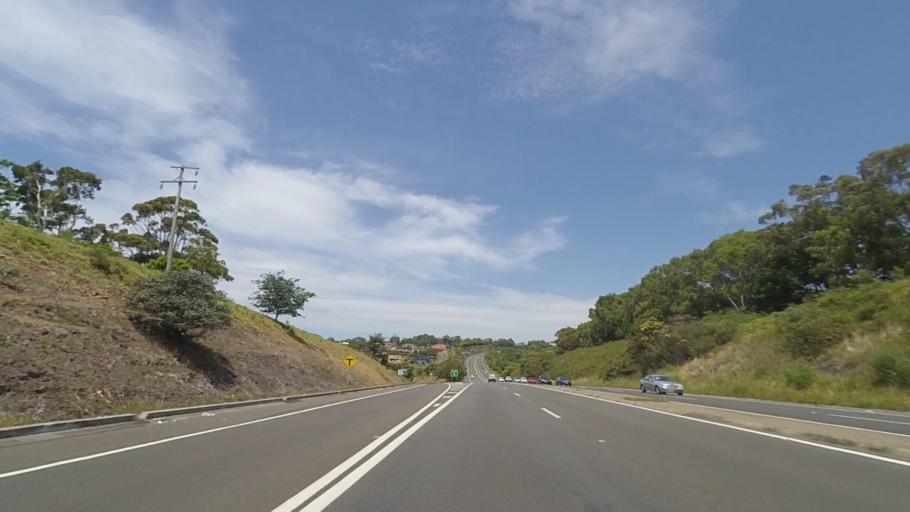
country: AU
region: New South Wales
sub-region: Kiama
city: Kiama
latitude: -34.6878
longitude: 150.8441
